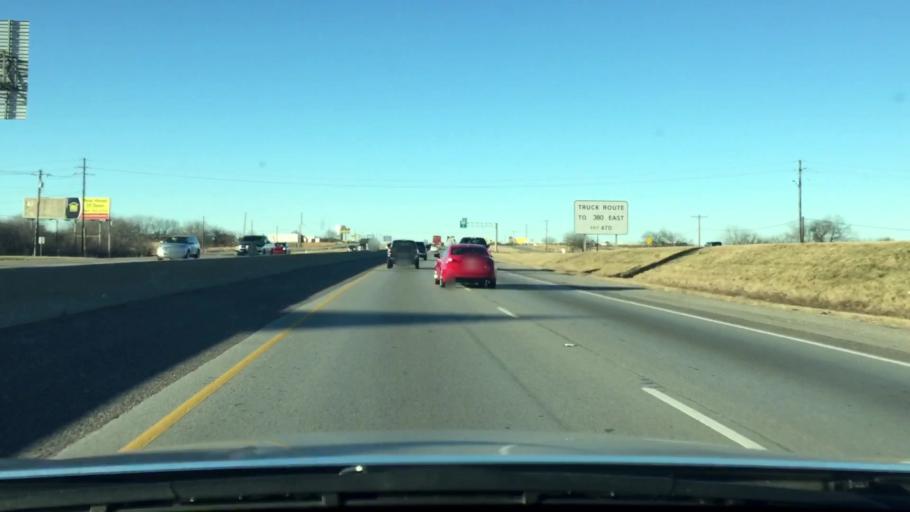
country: US
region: Texas
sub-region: Denton County
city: Denton
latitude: 33.2388
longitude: -97.1766
